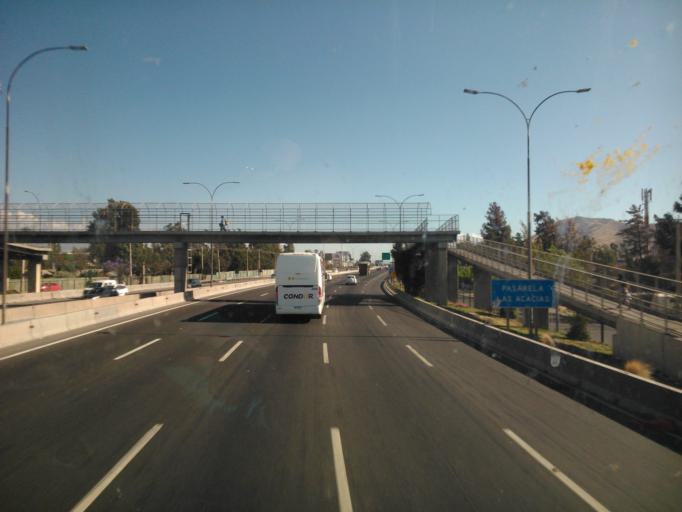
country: CL
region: Santiago Metropolitan
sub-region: Provincia de Maipo
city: San Bernardo
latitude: -33.5591
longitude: -70.7106
